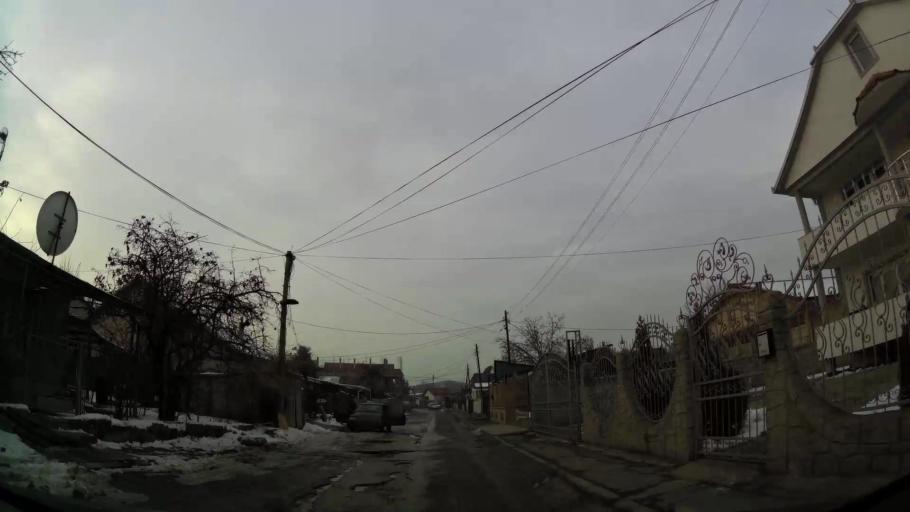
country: MK
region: Suto Orizari
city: Suto Orizare
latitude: 42.0445
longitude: 21.4288
